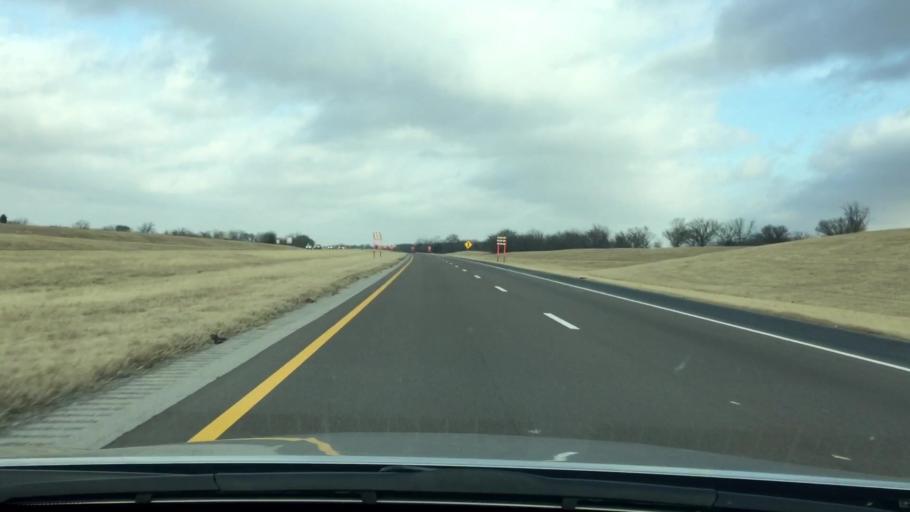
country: US
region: Oklahoma
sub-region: Garvin County
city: Maysville
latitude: 34.8269
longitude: -97.3093
